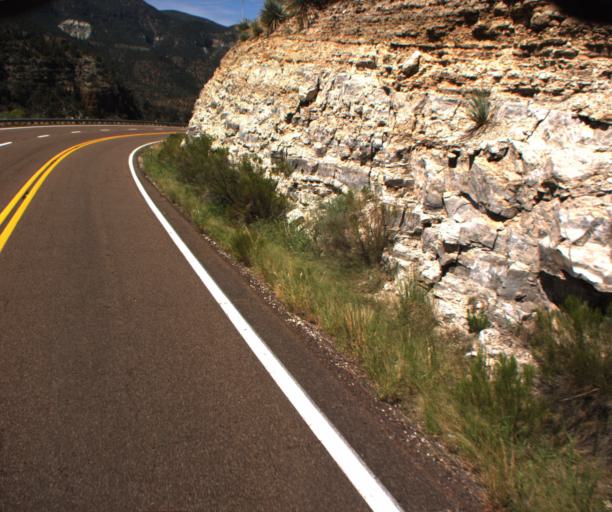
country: US
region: Arizona
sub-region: Navajo County
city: Cibecue
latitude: 33.7996
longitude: -110.5011
